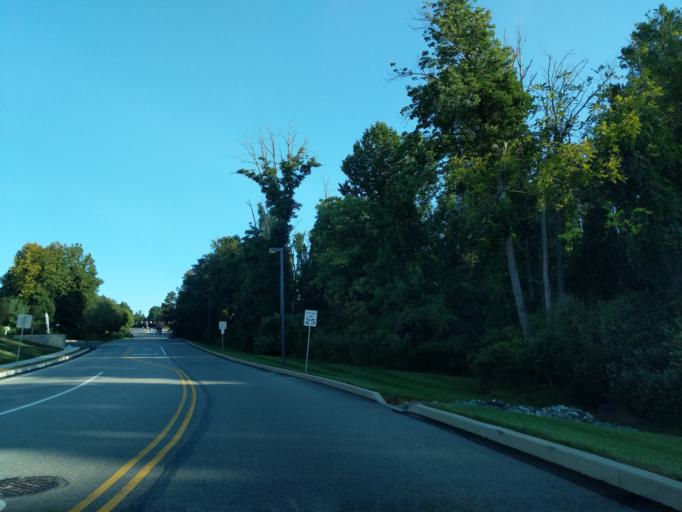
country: US
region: Pennsylvania
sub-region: Delaware County
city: Chester Heights
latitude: 39.8789
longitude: -75.5413
